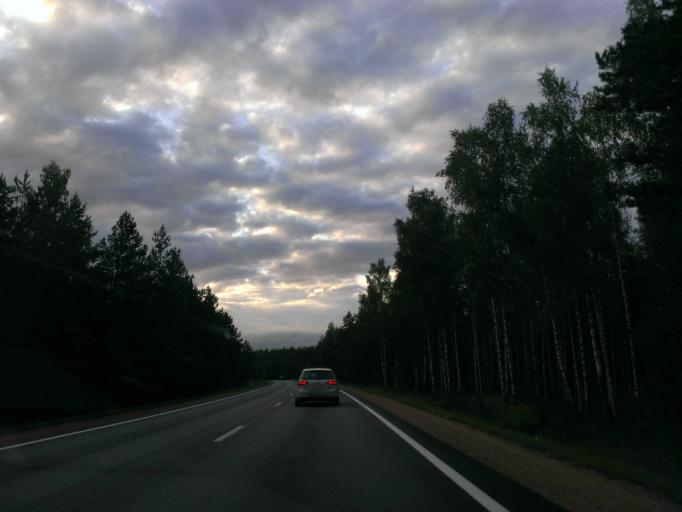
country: LV
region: Riga
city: Bergi
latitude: 56.9627
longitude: 24.3718
